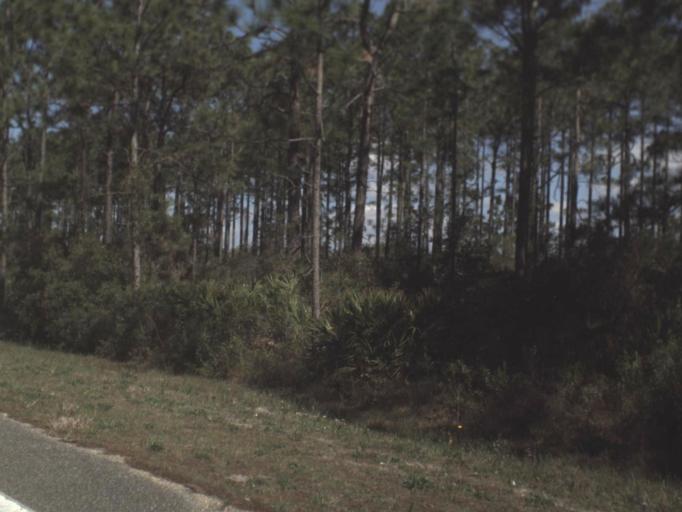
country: US
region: Florida
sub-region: Gulf County
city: Port Saint Joe
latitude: 29.7739
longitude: -85.2665
